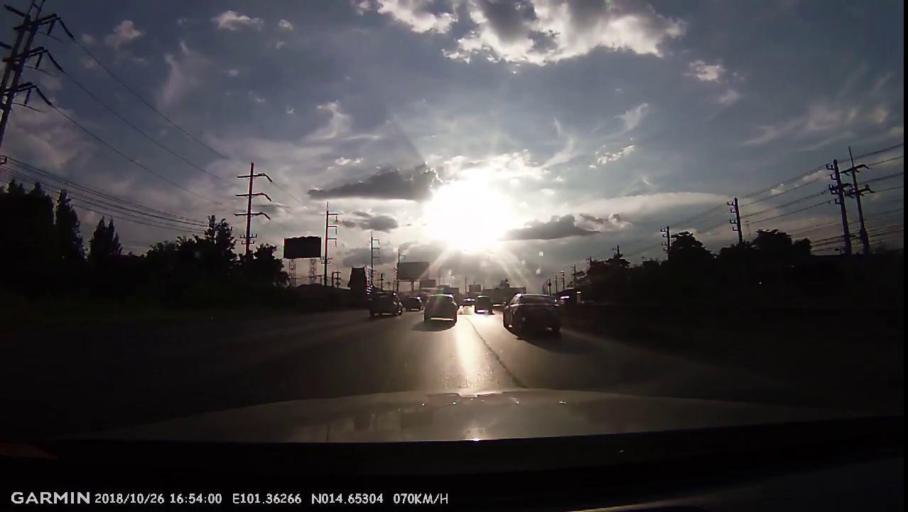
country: TH
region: Nakhon Ratchasima
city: Pak Chong
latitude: 14.6529
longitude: 101.3624
